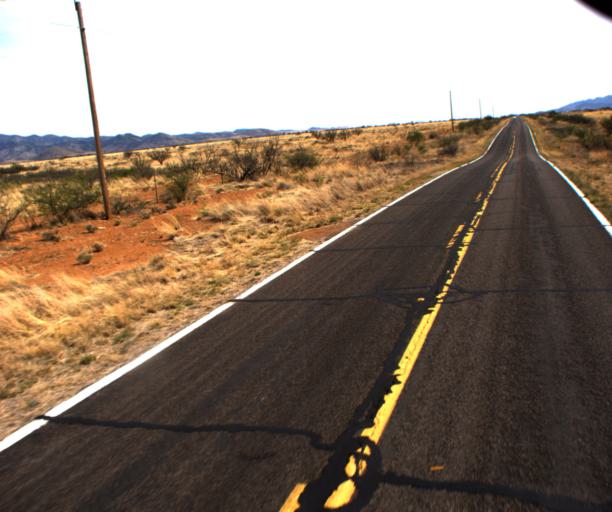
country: US
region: Arizona
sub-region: Cochise County
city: Willcox
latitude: 31.9114
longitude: -109.4915
